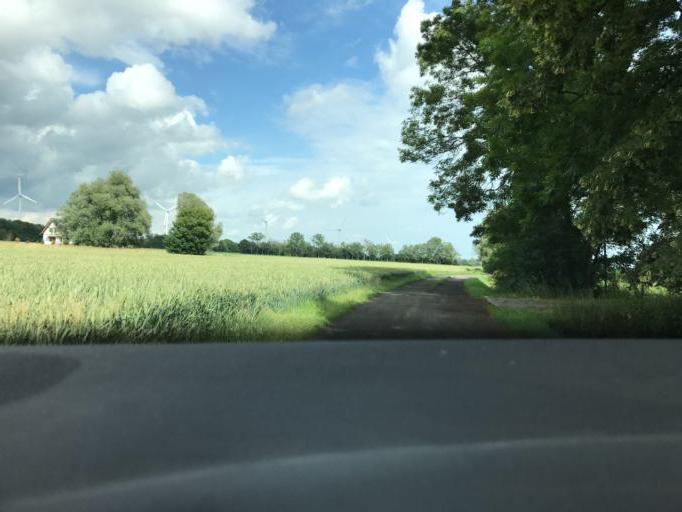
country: PL
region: Pomeranian Voivodeship
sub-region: Powiat gdanski
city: Pruszcz Gdanski
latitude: 54.2954
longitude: 18.7204
